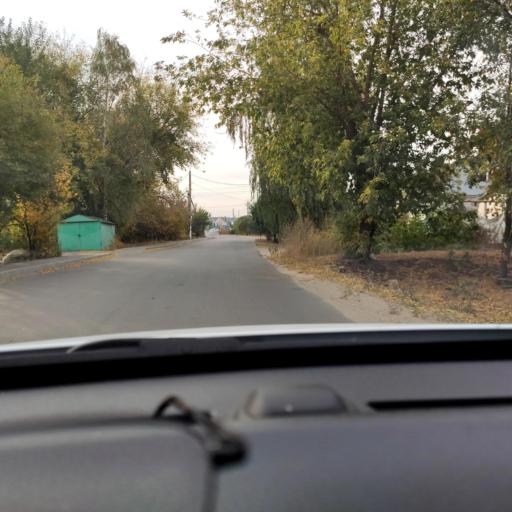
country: RU
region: Voronezj
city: Somovo
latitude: 51.6864
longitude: 39.3203
